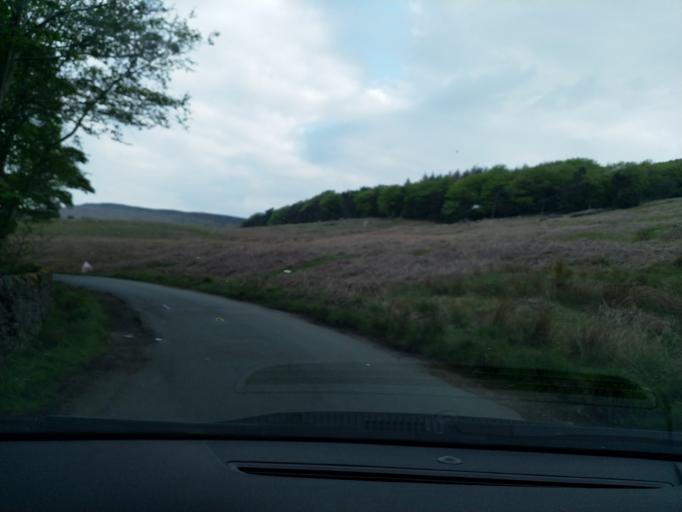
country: GB
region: England
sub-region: Derbyshire
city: Hathersage
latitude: 53.3486
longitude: -1.6404
